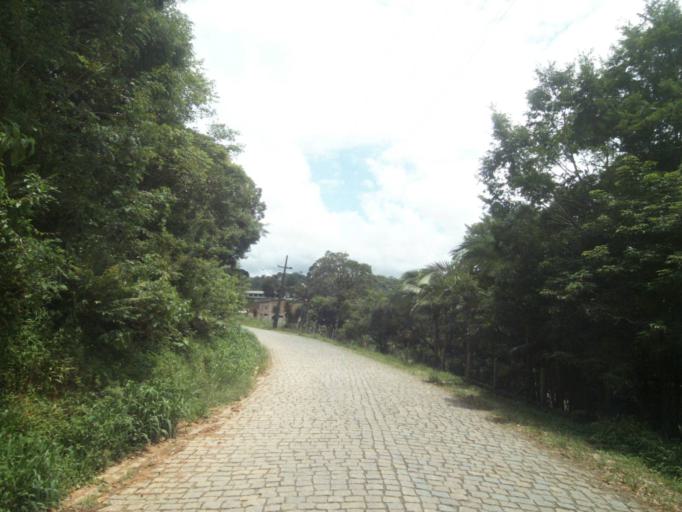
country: BR
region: Parana
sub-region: Campina Grande Do Sul
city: Campina Grande do Sul
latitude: -25.1095
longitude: -48.8077
